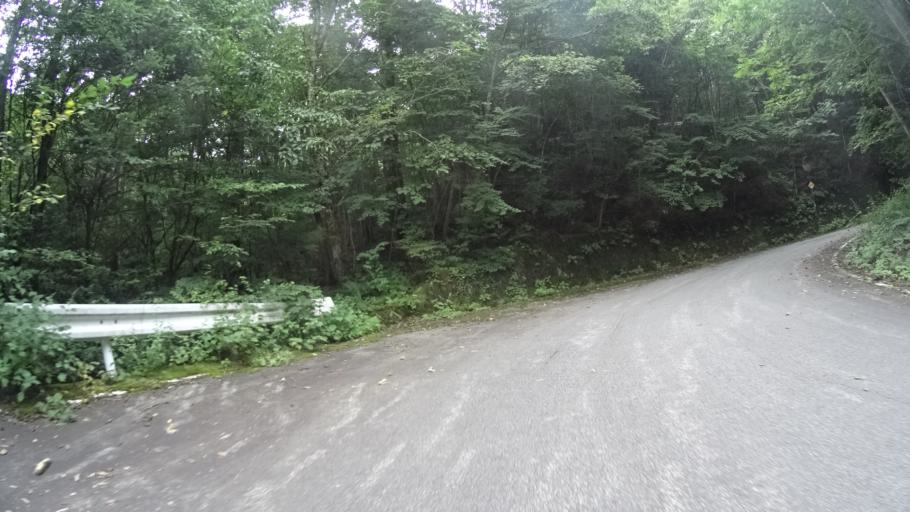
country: JP
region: Yamanashi
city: Kofu-shi
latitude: 35.8065
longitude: 138.6174
